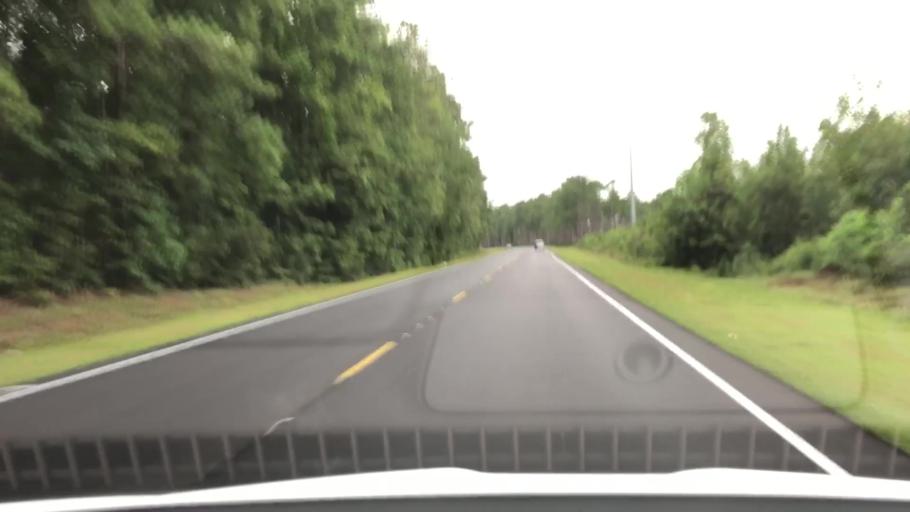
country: US
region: North Carolina
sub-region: Onslow County
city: Swansboro
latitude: 34.7693
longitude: -77.0969
